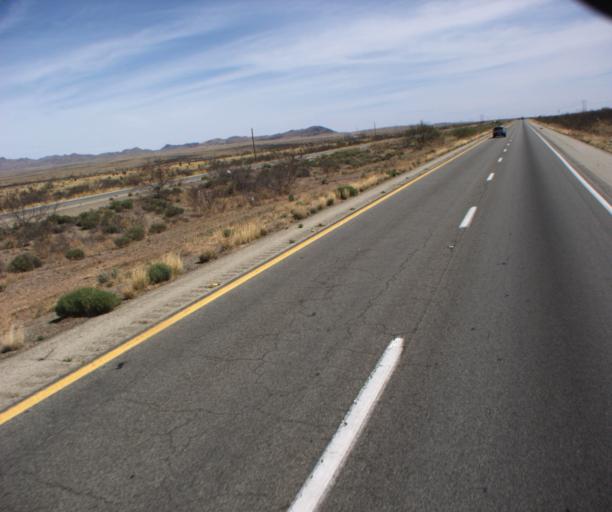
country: US
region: Arizona
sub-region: Cochise County
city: Willcox
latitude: 32.3279
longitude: -109.7712
